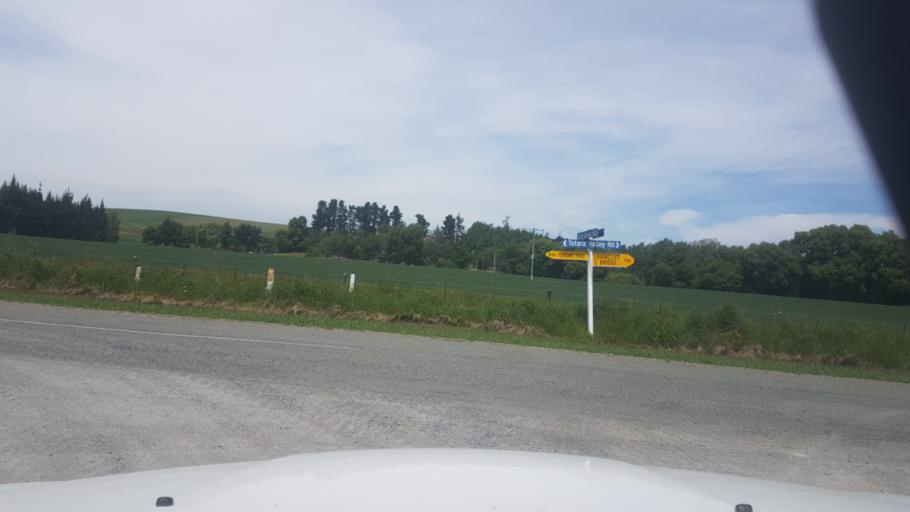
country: NZ
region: Canterbury
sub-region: Timaru District
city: Pleasant Point
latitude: -44.2282
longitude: 171.0506
